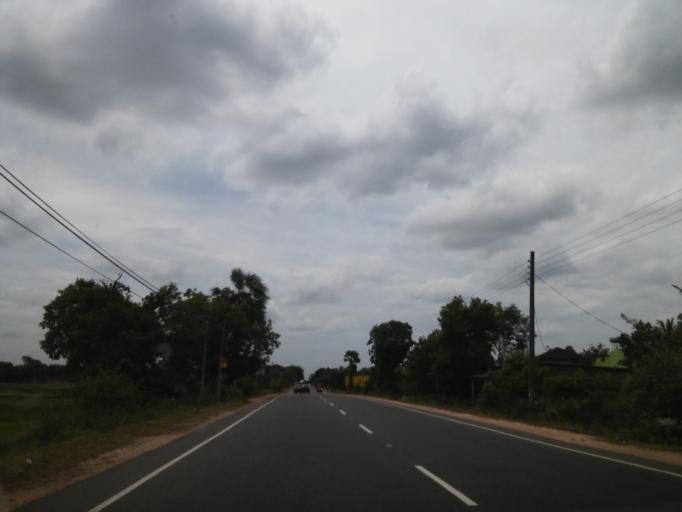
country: LK
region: Eastern Province
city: Trincomalee
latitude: 8.4730
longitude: 81.0768
